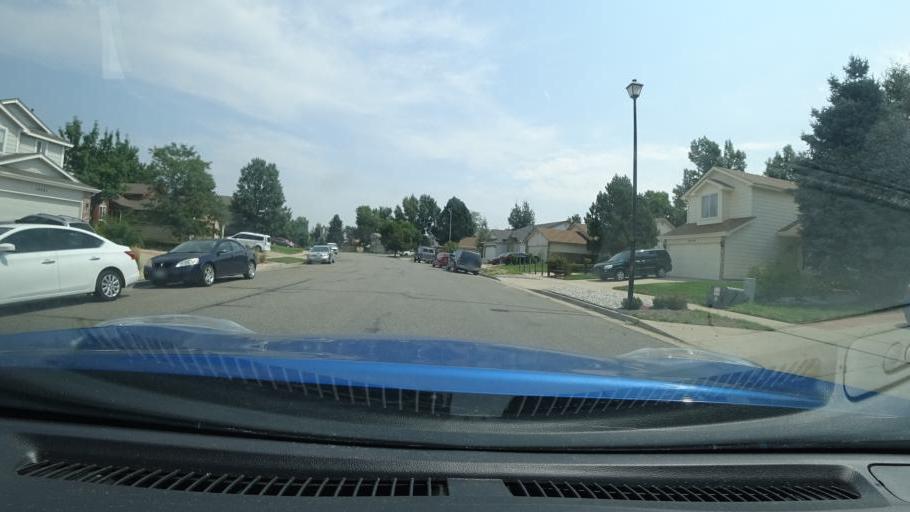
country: US
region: Colorado
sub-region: Adams County
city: Aurora
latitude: 39.7768
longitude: -104.7597
